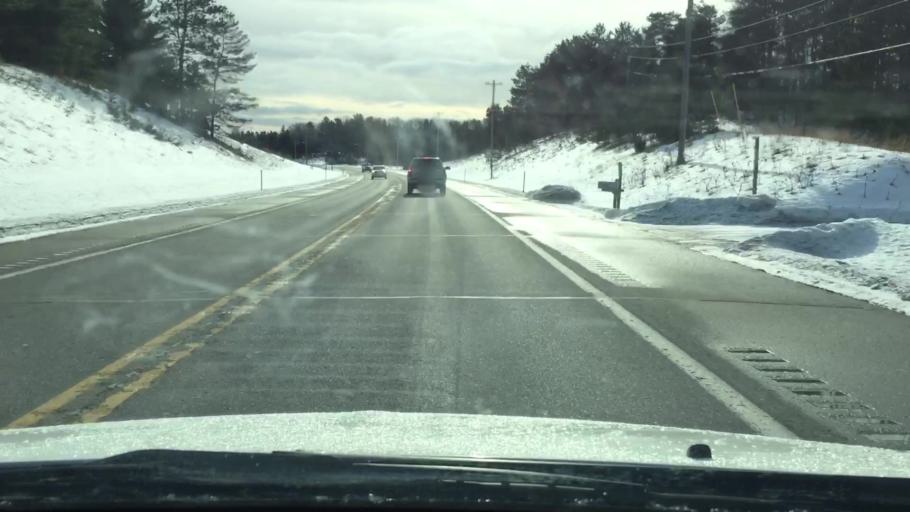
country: US
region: Michigan
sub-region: Wexford County
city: Manton
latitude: 44.5801
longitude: -85.3618
